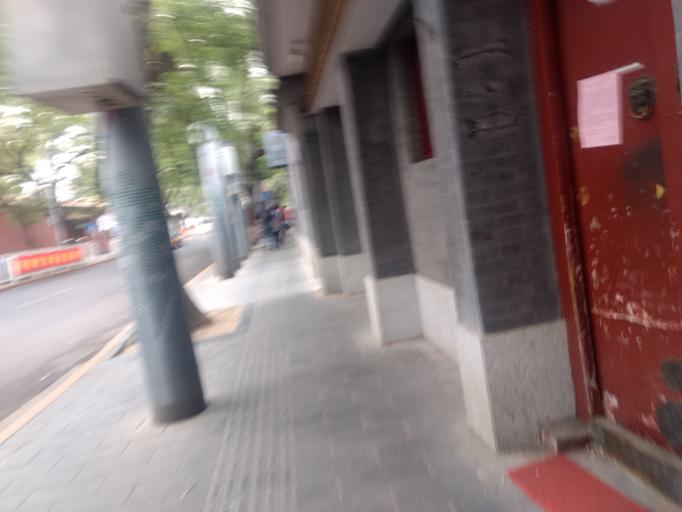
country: CN
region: Beijing
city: Beijing
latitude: 39.9085
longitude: 116.3969
